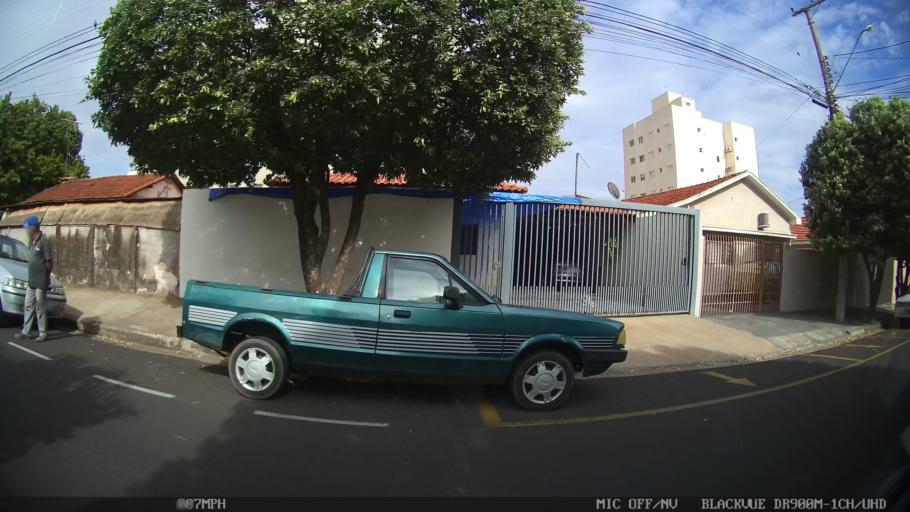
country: BR
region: Sao Paulo
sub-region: Sao Jose Do Rio Preto
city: Sao Jose do Rio Preto
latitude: -20.8339
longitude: -49.3809
